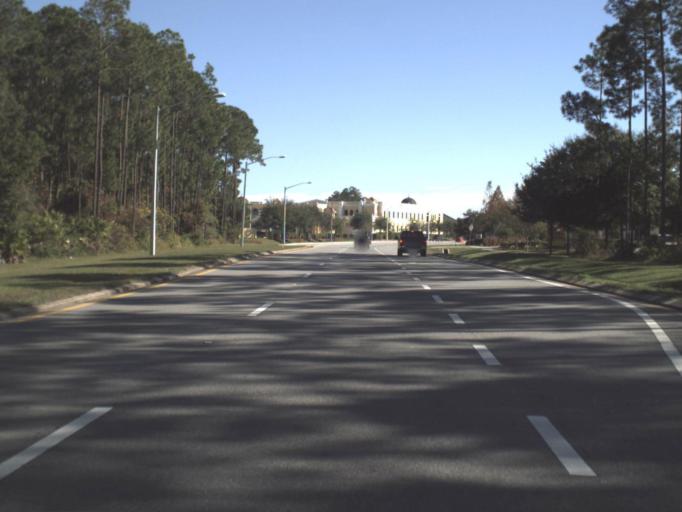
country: US
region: Florida
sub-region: Flagler County
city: Palm Coast
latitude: 29.5514
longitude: -81.2453
